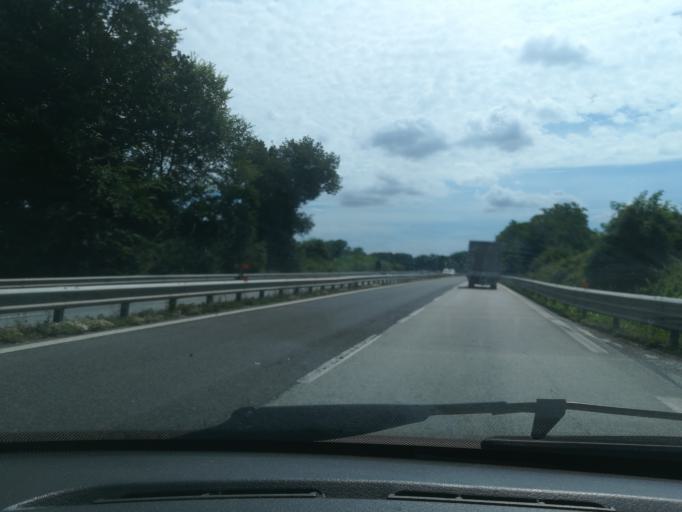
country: IT
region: The Marches
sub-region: Provincia di Macerata
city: Corridonia
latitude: 43.2685
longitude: 13.5175
